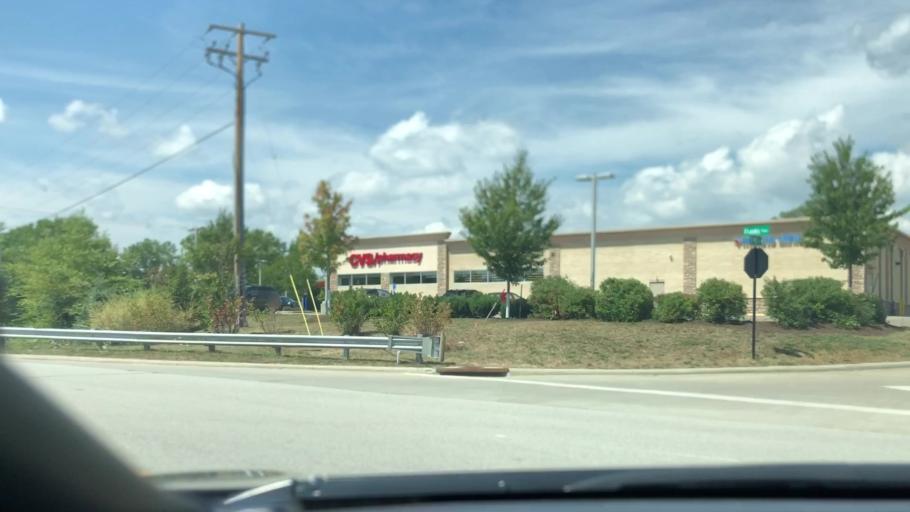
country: US
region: Ohio
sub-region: Summit County
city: Green
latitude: 40.9589
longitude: -81.4641
